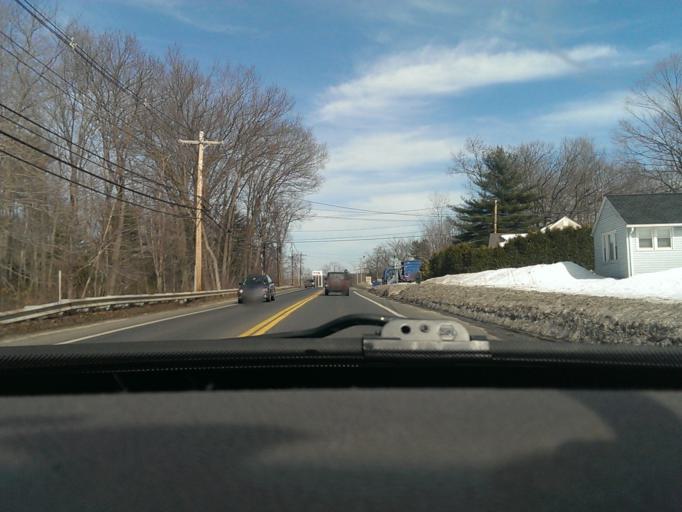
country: US
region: Massachusetts
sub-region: Hampden County
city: Three Rivers
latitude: 42.1591
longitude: -72.3592
